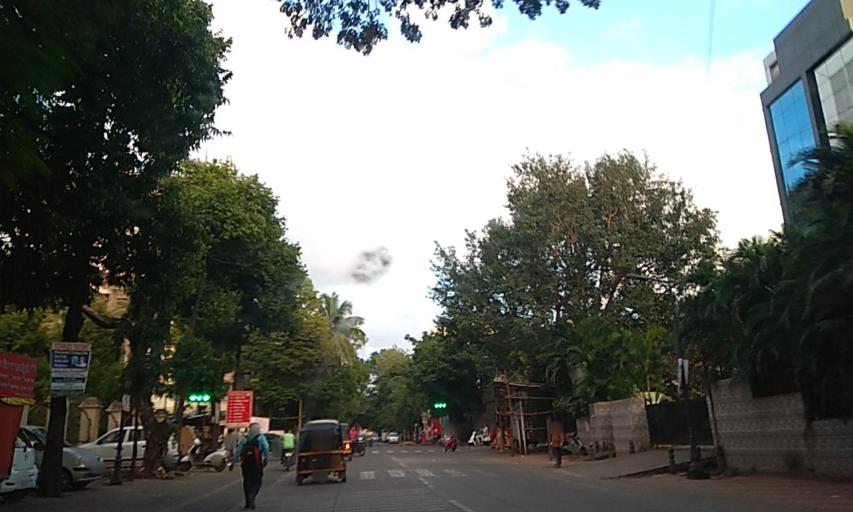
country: IN
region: Maharashtra
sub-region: Pune Division
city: Pune
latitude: 18.4924
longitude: 73.8534
